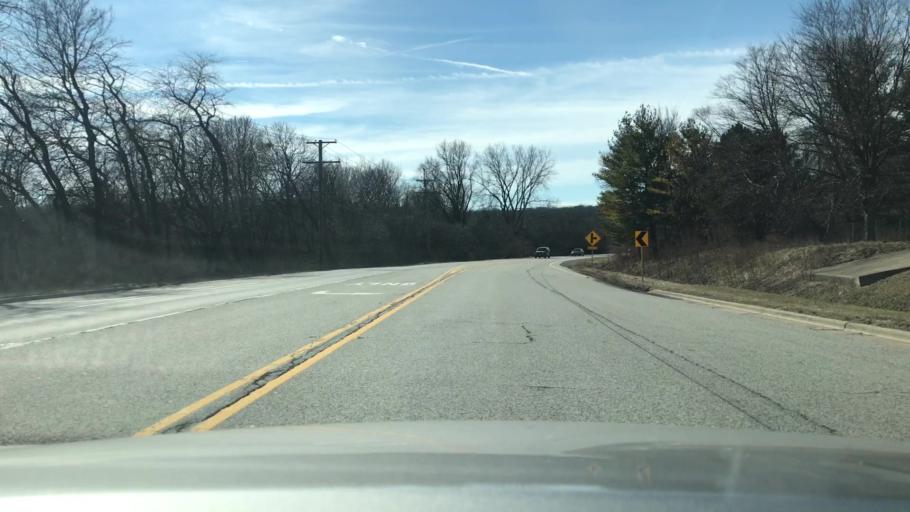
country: US
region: Illinois
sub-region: DuPage County
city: Lisle
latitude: 41.8273
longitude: -88.0546
